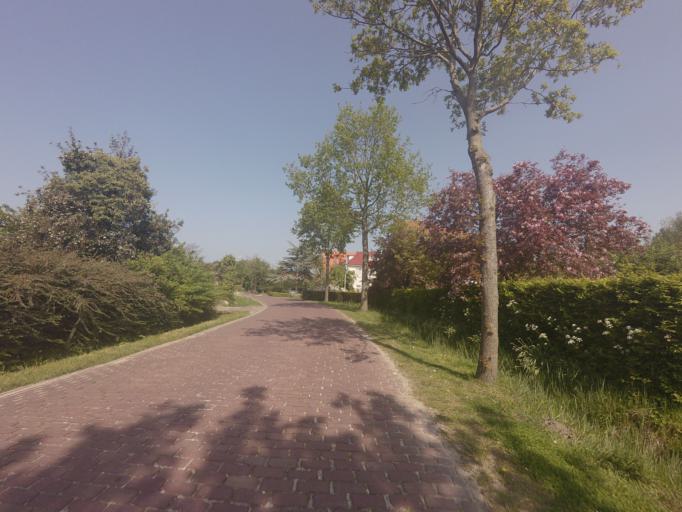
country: NL
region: Zeeland
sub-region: Gemeente Middelburg
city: Middelburg
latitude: 51.5667
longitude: 3.5439
